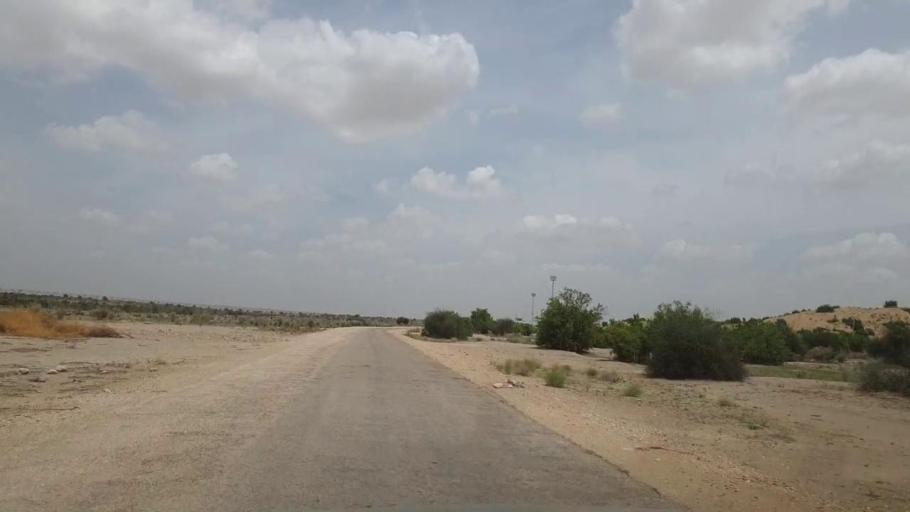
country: PK
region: Sindh
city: Kot Diji
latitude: 27.2021
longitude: 69.1482
